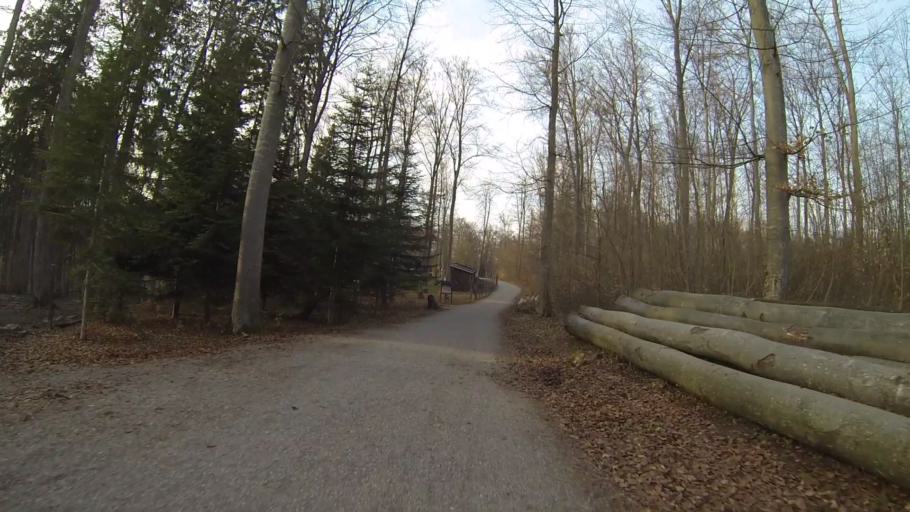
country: DE
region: Baden-Wuerttemberg
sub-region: Regierungsbezirk Stuttgart
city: Heidenheim an der Brenz
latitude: 48.6730
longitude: 10.1377
